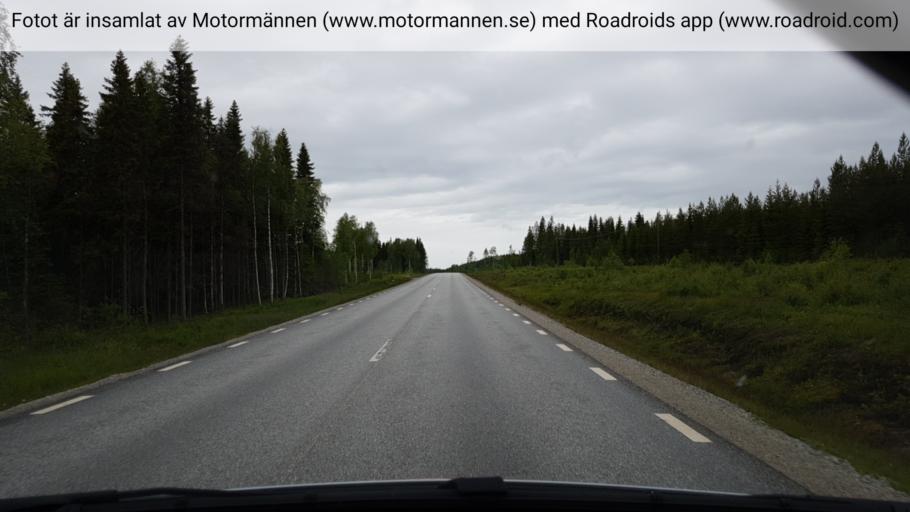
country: SE
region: Vaesterbotten
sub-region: Vindelns Kommun
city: Vindeln
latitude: 64.1915
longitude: 19.4615
